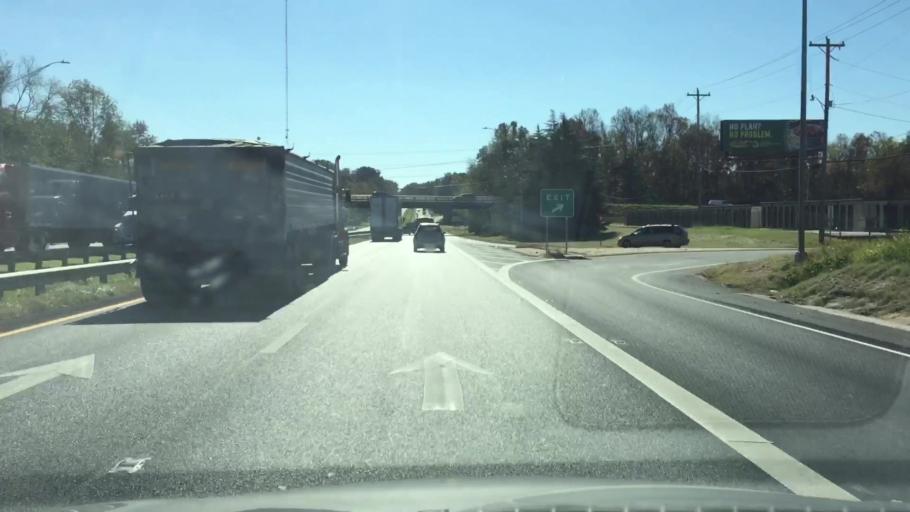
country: US
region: North Carolina
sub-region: Guilford County
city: Greensboro
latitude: 36.1079
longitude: -79.7602
